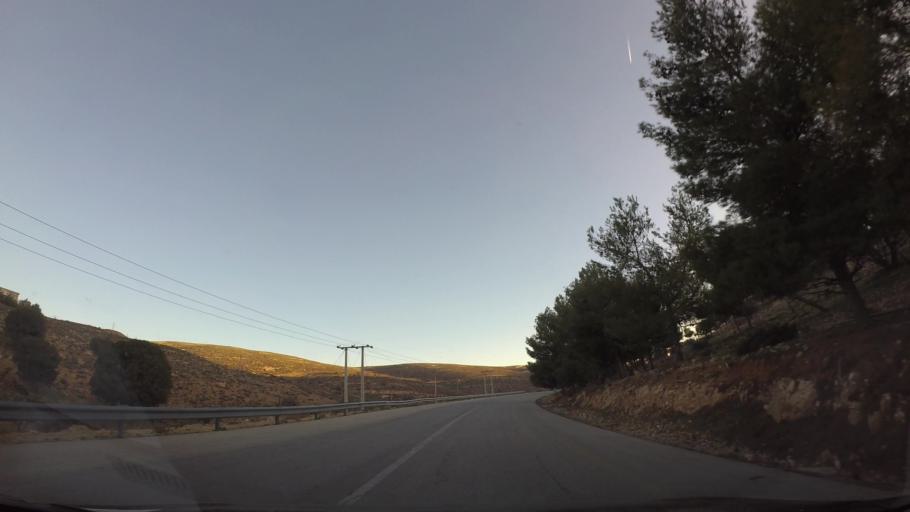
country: JO
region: Ma'an
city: Petra
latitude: 30.4130
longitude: 35.5082
